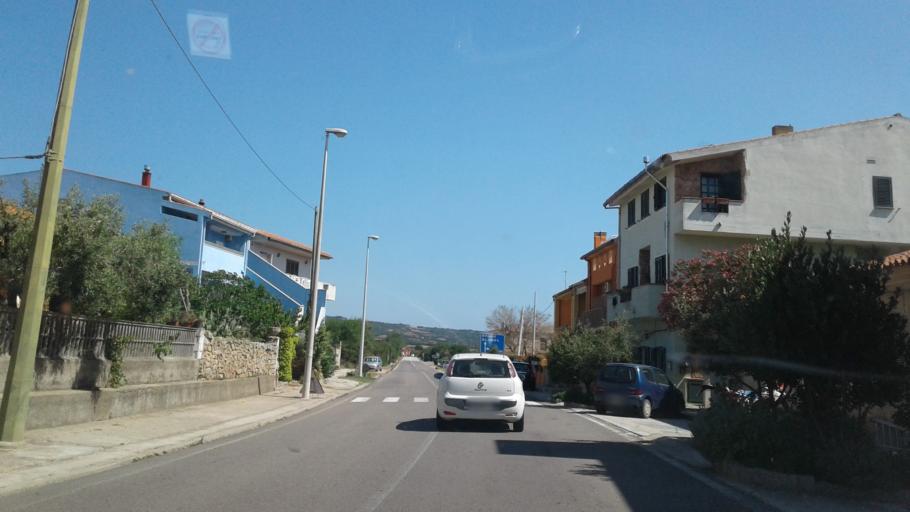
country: IT
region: Sardinia
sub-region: Provincia di Olbia-Tempio
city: Luogosanto
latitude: 41.1099
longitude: 9.2621
